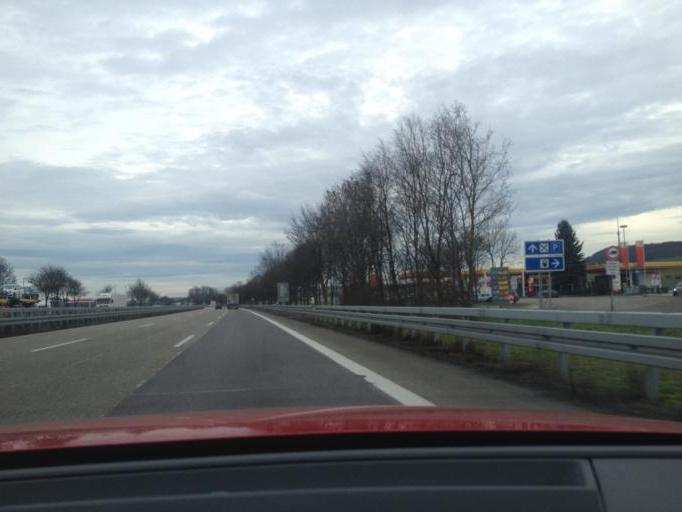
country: DE
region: Baden-Wuerttemberg
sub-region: Regierungsbezirk Stuttgart
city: Waldenburg
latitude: 49.2067
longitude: 9.6365
